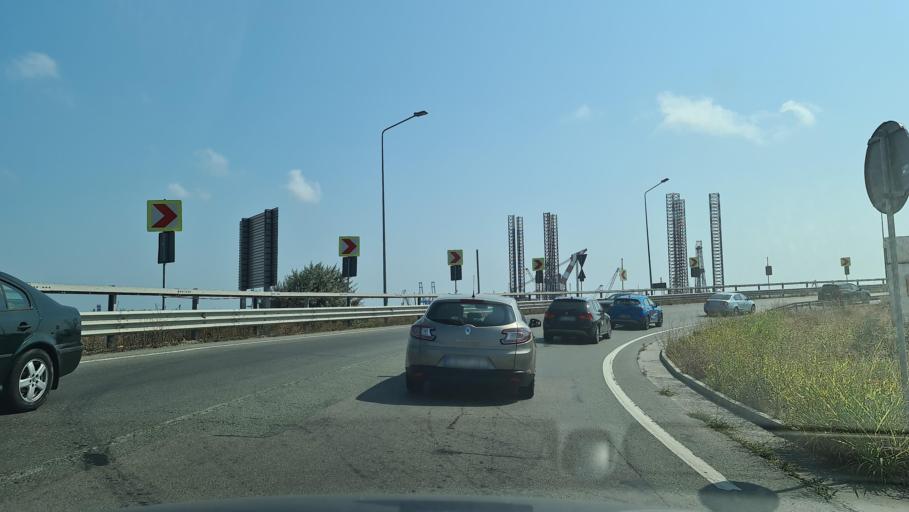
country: RO
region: Constanta
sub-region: Comuna Agigea
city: Agigea
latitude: 44.0969
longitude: 28.6387
